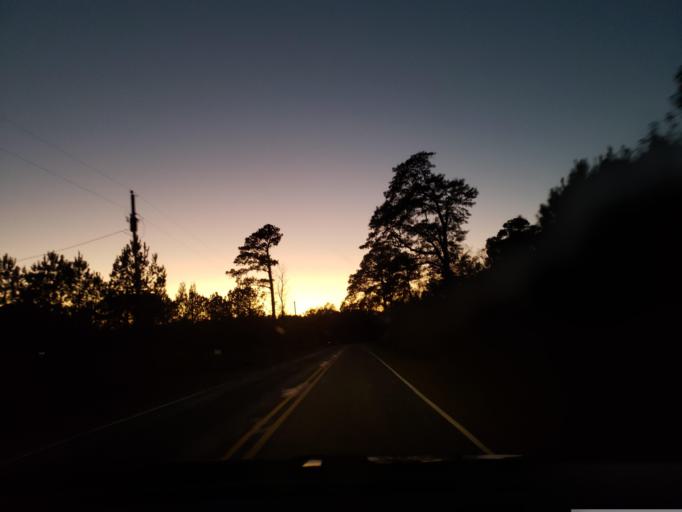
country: US
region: North Carolina
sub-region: Duplin County
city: Kenansville
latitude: 34.9416
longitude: -77.9577
